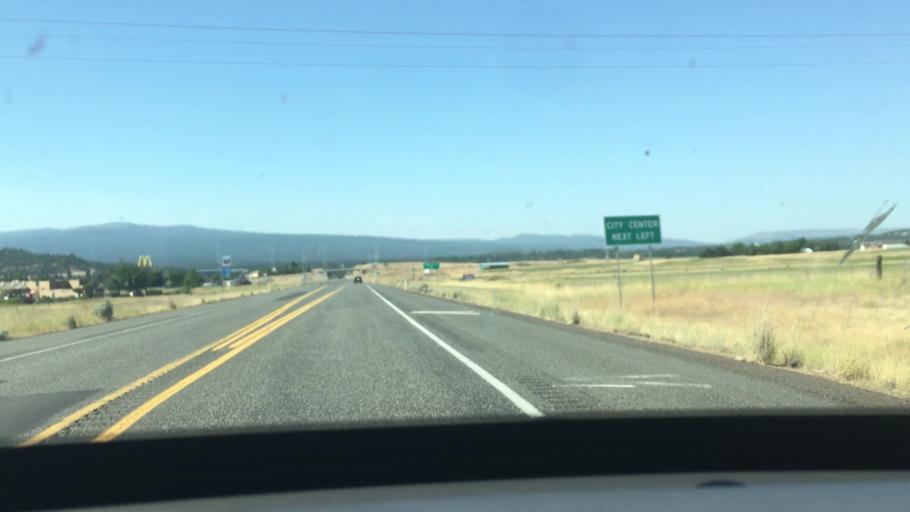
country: US
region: Washington
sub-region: Klickitat County
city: Goldendale
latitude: 45.8098
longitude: -120.8079
